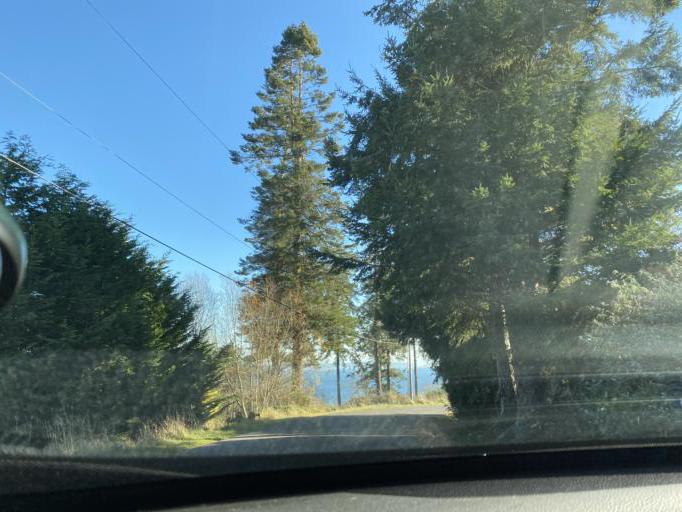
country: US
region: Washington
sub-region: Island County
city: Camano
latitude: 48.1303
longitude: -122.5661
